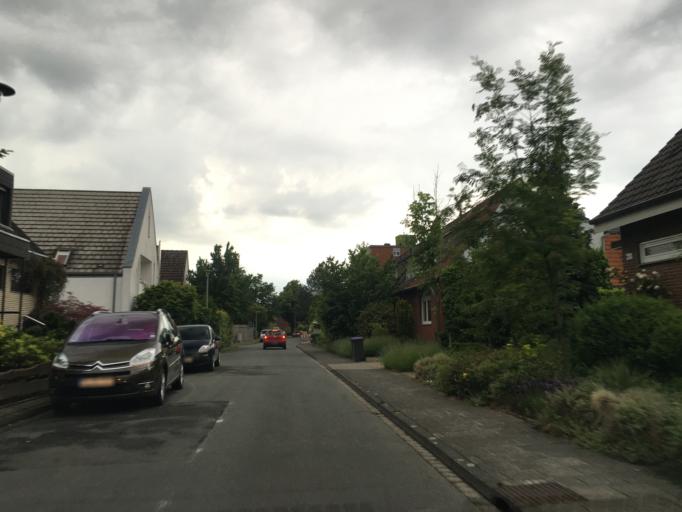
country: DE
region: North Rhine-Westphalia
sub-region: Regierungsbezirk Munster
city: Muenster
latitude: 51.9633
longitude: 7.5830
